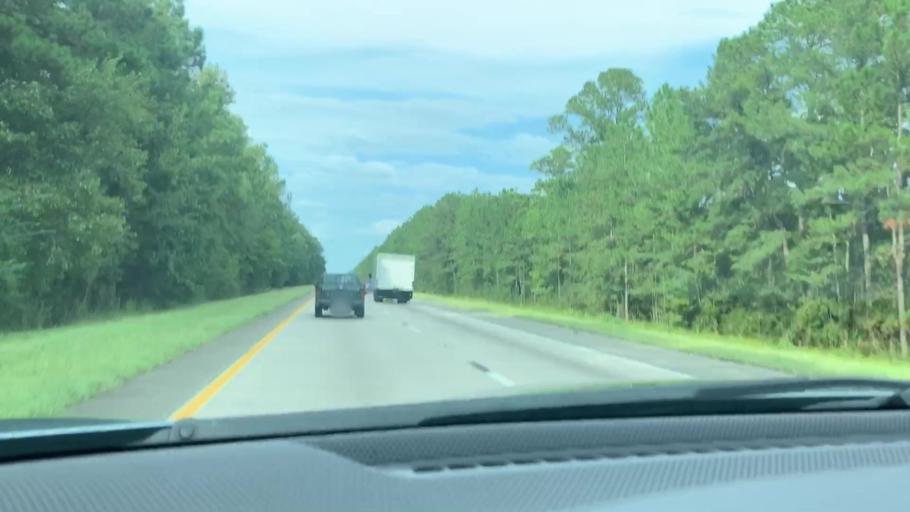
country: US
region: South Carolina
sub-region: Colleton County
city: Walterboro
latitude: 32.9903
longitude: -80.6717
